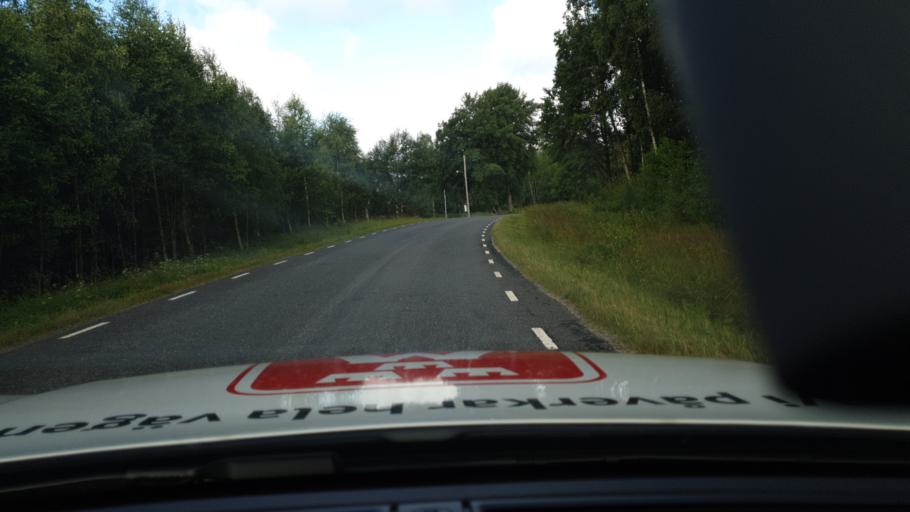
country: SE
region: Vaestra Goetaland
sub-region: Falkopings Kommun
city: Floby
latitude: 58.1255
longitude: 13.3925
